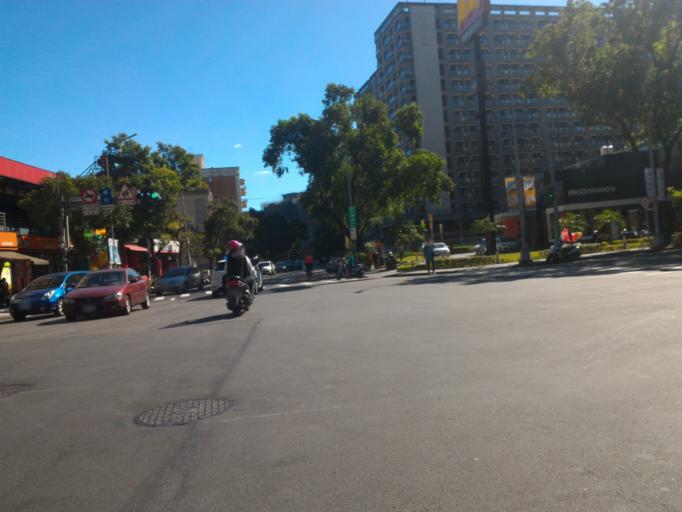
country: TW
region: Taiwan
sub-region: Taoyuan
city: Taoyuan
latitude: 24.9428
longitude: 121.3754
